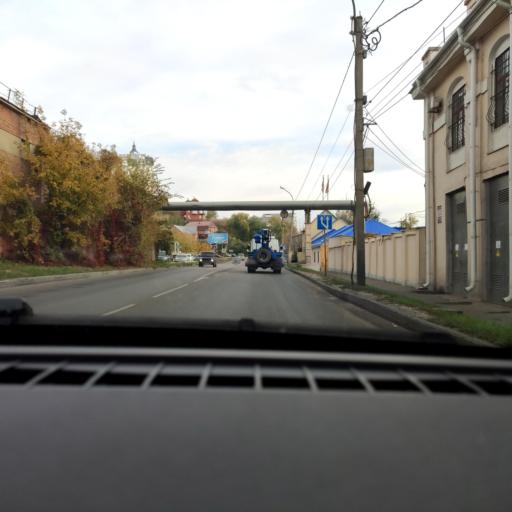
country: RU
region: Voronezj
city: Voronezh
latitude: 51.6597
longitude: 39.2159
